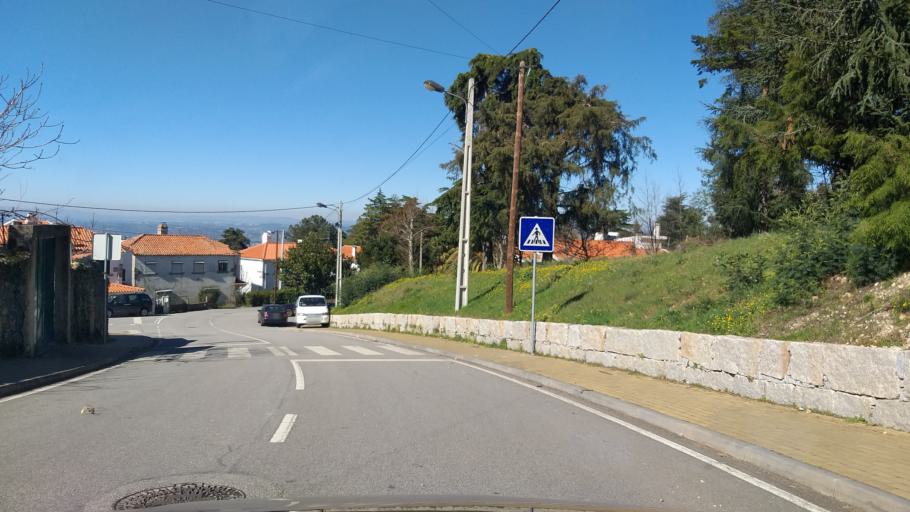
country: PT
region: Guarda
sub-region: Manteigas
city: Manteigas
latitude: 40.4891
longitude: -7.5917
